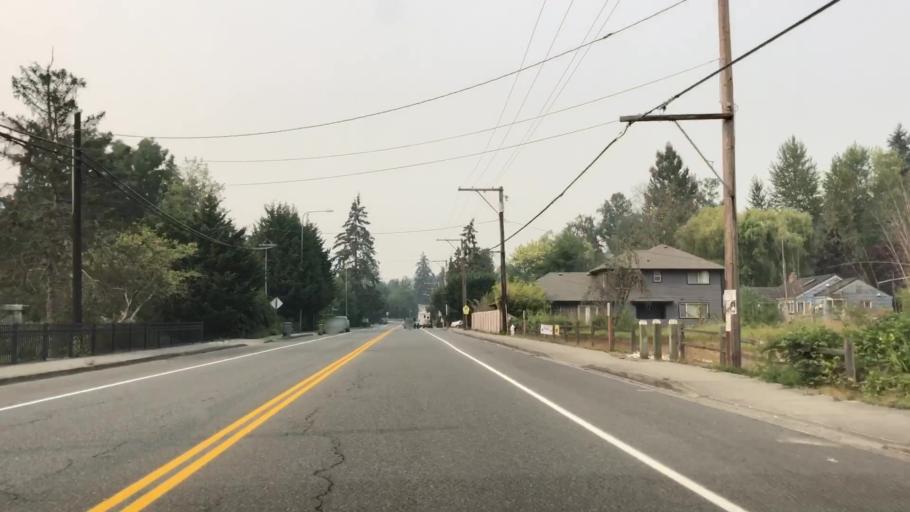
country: US
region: Washington
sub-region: King County
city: Kenmore
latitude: 47.7649
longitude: -122.2425
